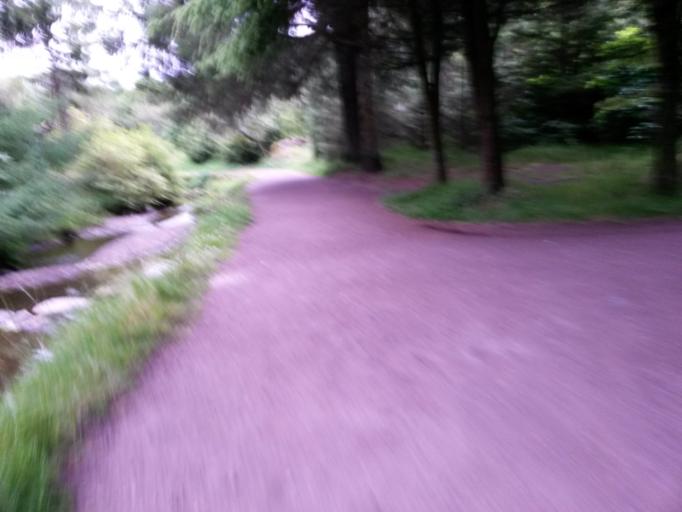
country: FO
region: Streymoy
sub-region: Torshavn
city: Torshavn
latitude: 62.0166
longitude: -6.7783
